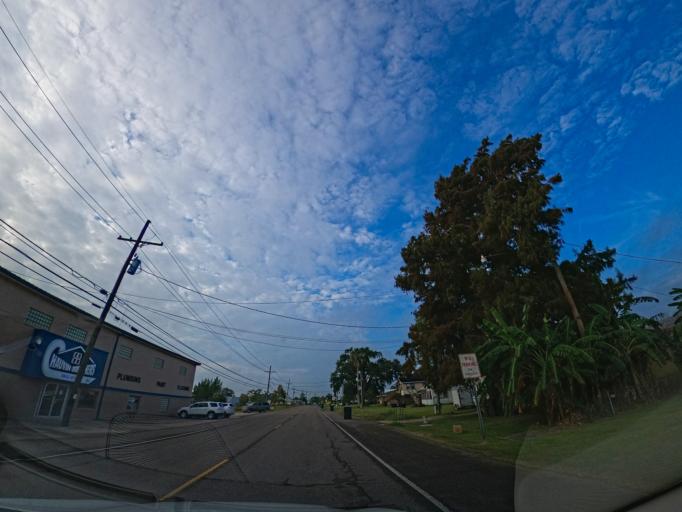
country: US
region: Louisiana
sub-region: Terrebonne Parish
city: Chauvin
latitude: 29.4348
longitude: -90.5962
